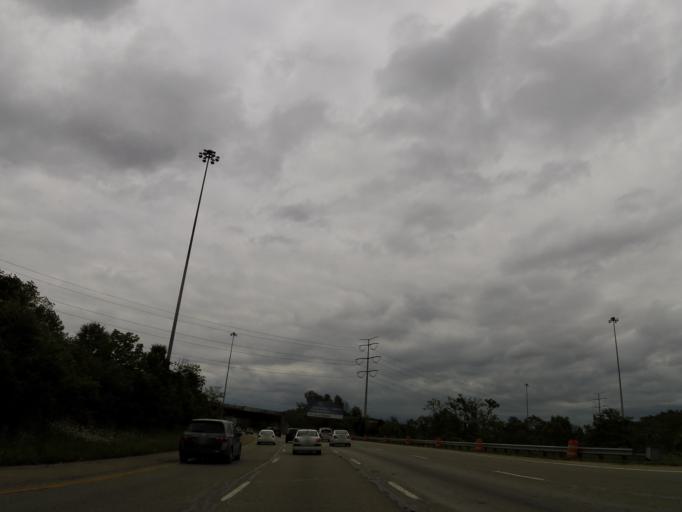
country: US
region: Ohio
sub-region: Hamilton County
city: Golf Manor
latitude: 39.1652
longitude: -84.4269
